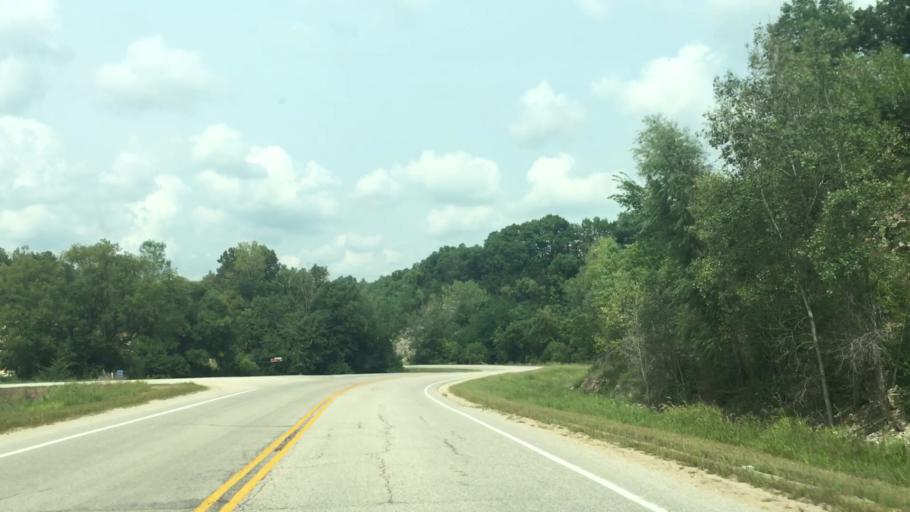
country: US
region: Minnesota
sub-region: Fillmore County
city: Preston
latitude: 43.7050
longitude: -91.9704
